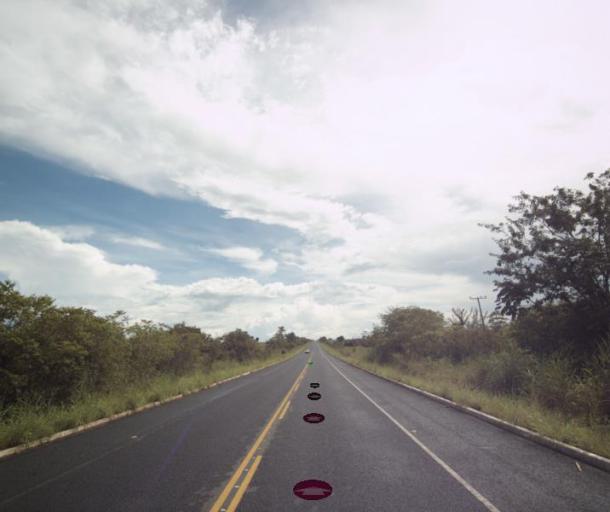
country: BR
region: Goias
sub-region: Sao Miguel Do Araguaia
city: Sao Miguel do Araguaia
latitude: -13.2965
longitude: -50.2401
